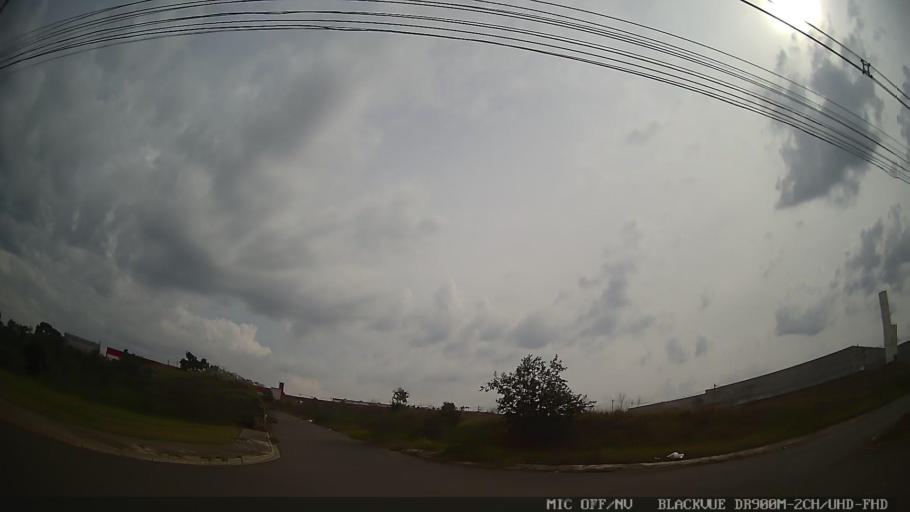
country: BR
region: Sao Paulo
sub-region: Indaiatuba
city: Indaiatuba
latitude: -23.1172
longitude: -47.2692
